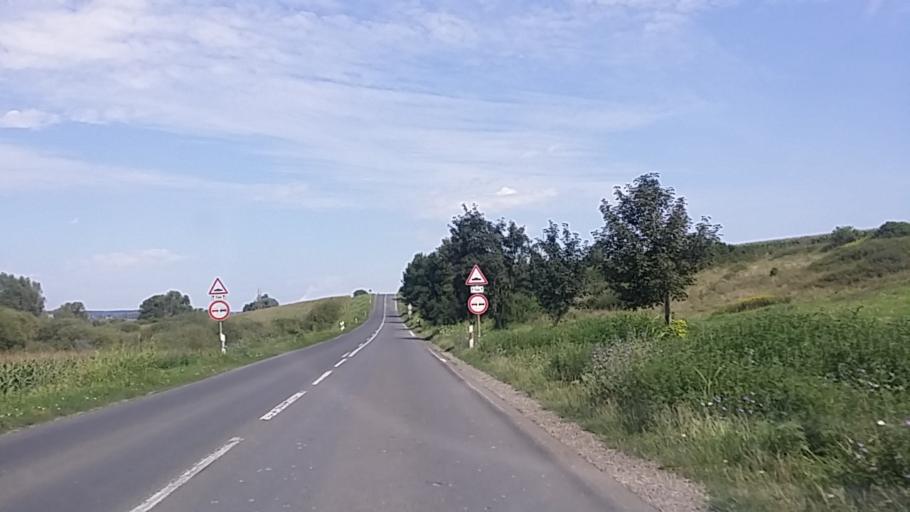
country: HU
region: Baranya
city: Sasd
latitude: 46.2268
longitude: 18.1217
